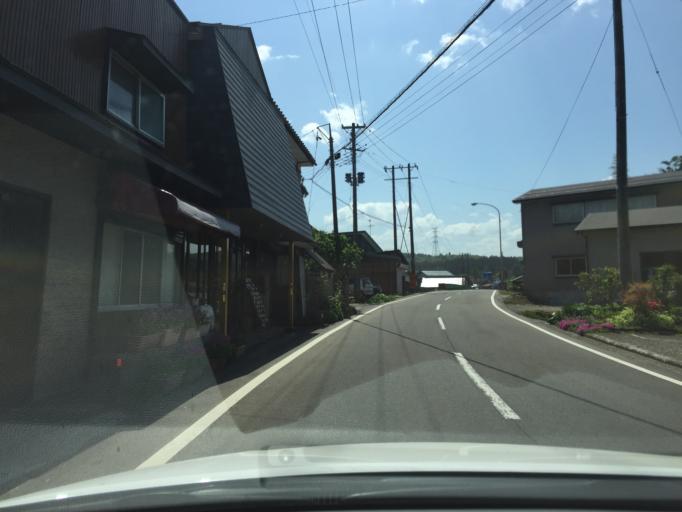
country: JP
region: Niigata
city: Tochio-honcho
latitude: 37.5469
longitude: 139.0900
